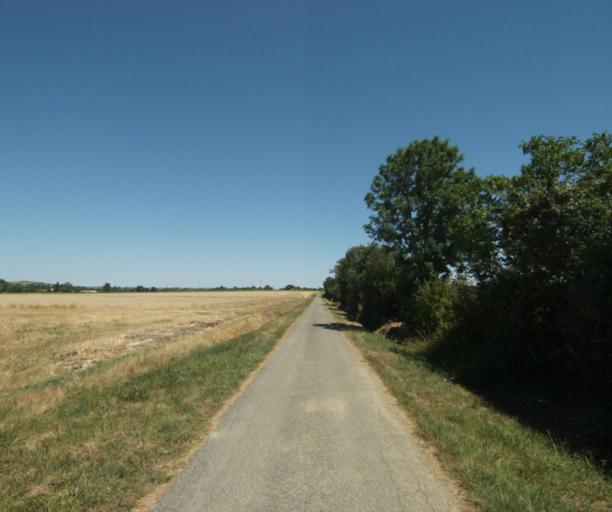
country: FR
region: Midi-Pyrenees
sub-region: Departement de la Haute-Garonne
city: Saint-Felix-Lauragais
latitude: 43.4567
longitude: 1.9309
